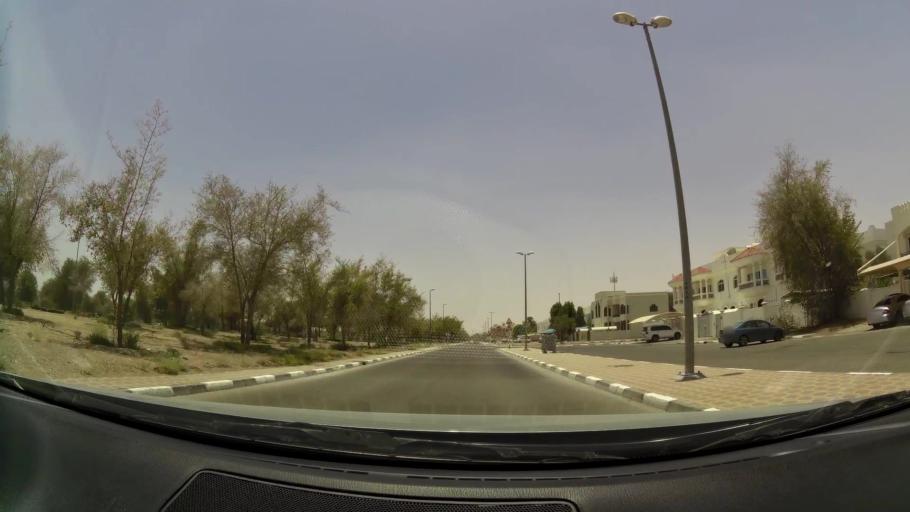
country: OM
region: Al Buraimi
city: Al Buraymi
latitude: 24.2597
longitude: 55.7256
